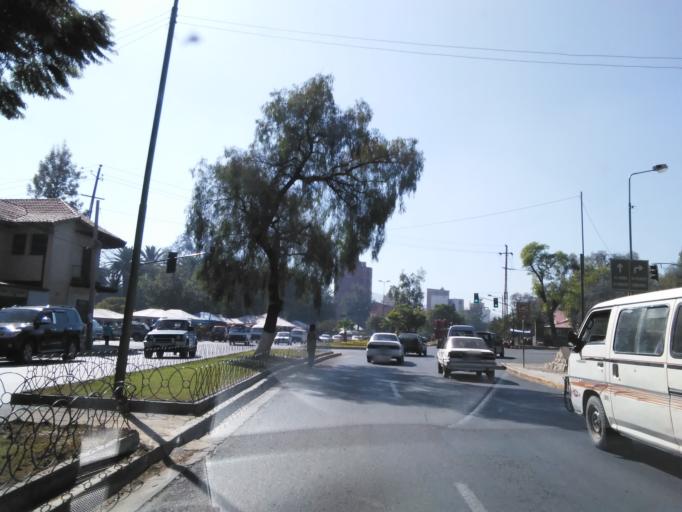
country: BO
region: Cochabamba
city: Cochabamba
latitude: -17.3996
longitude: -66.1608
